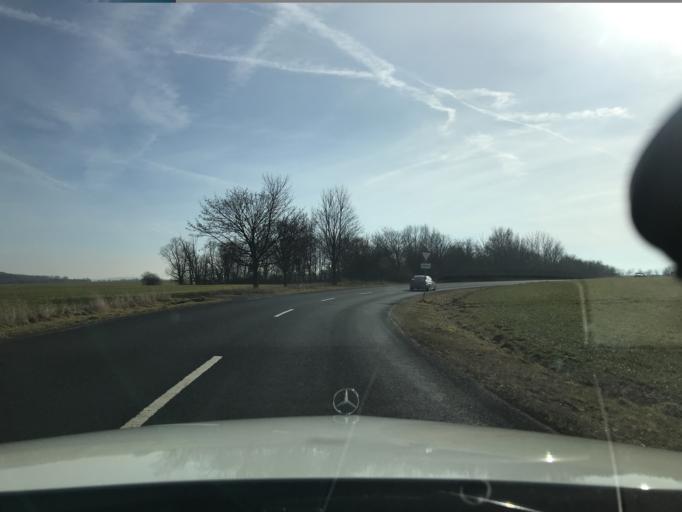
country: DE
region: Thuringia
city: Ernstroda
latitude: 50.8976
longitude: 10.6375
